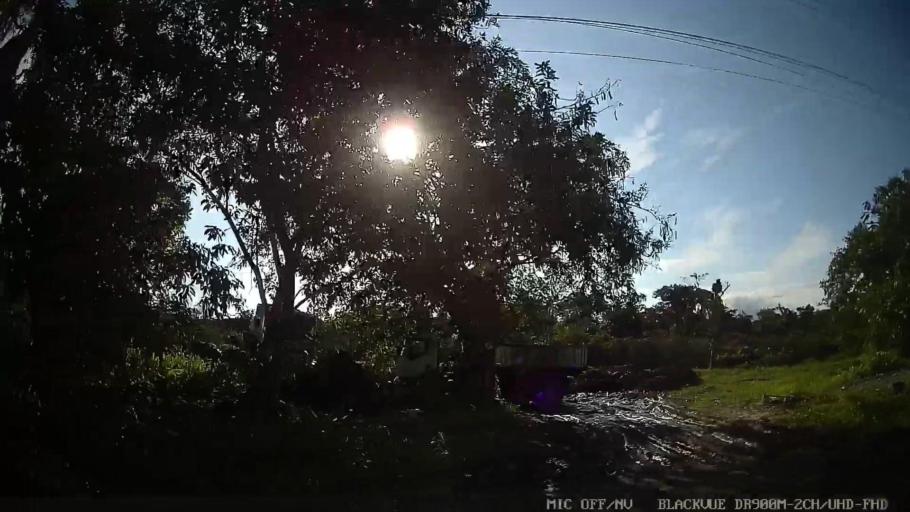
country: BR
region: Sao Paulo
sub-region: Itanhaem
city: Itanhaem
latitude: -24.1697
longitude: -46.8175
